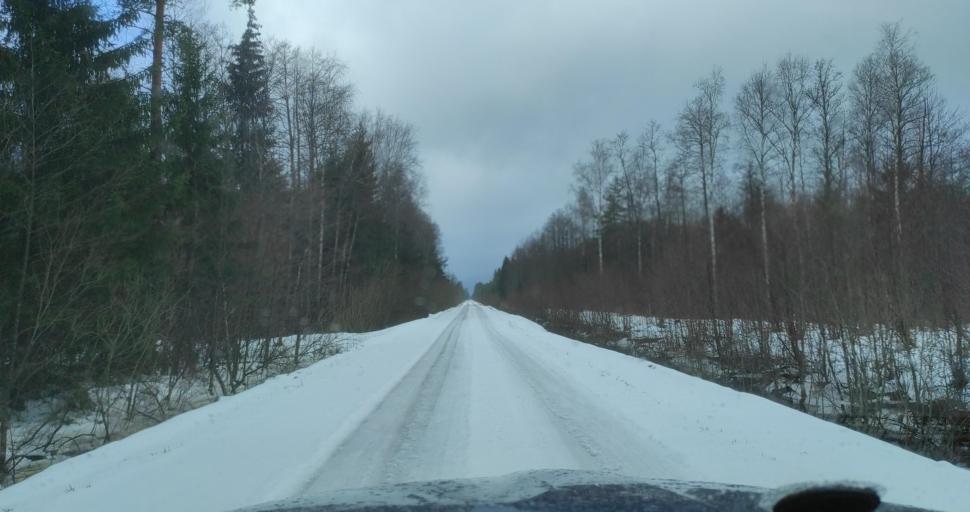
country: LV
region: Dundaga
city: Dundaga
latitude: 57.3970
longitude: 22.1162
